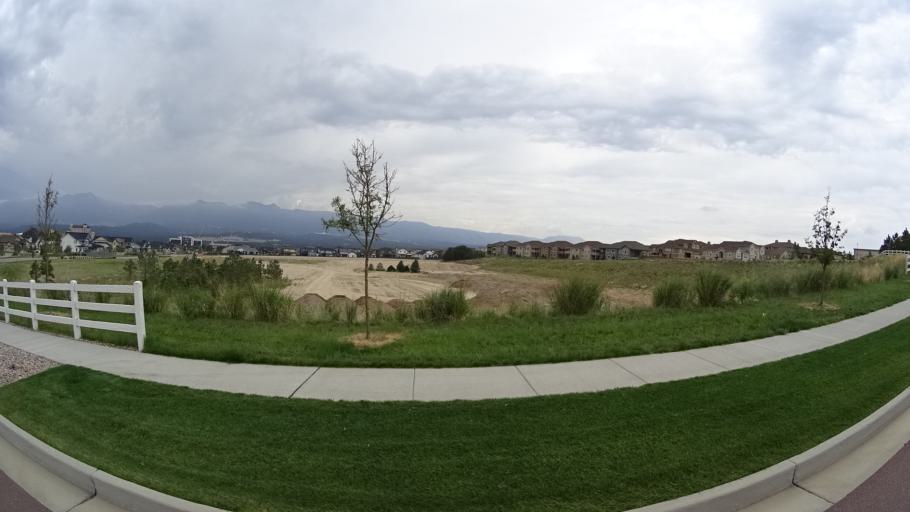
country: US
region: Colorado
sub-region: El Paso County
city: Gleneagle
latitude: 39.0009
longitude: -104.7991
